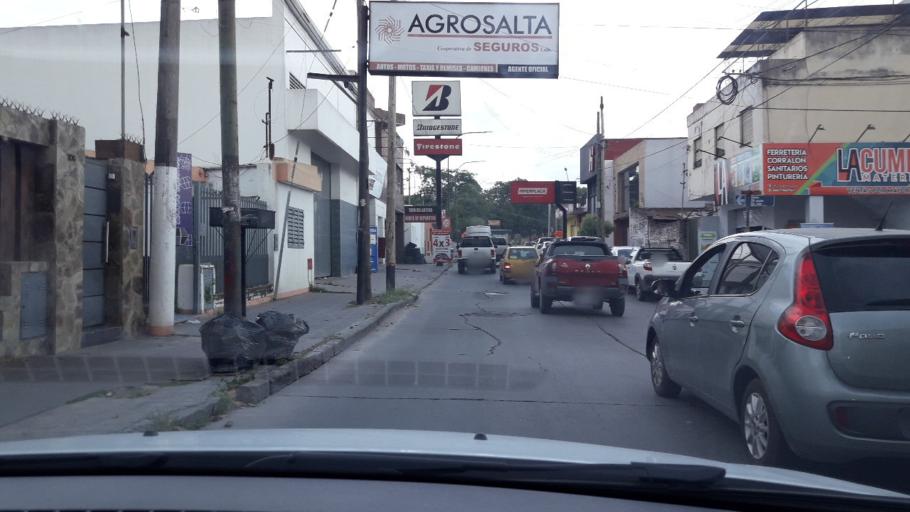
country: AR
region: Jujuy
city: San Salvador de Jujuy
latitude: -24.1914
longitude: -65.2913
